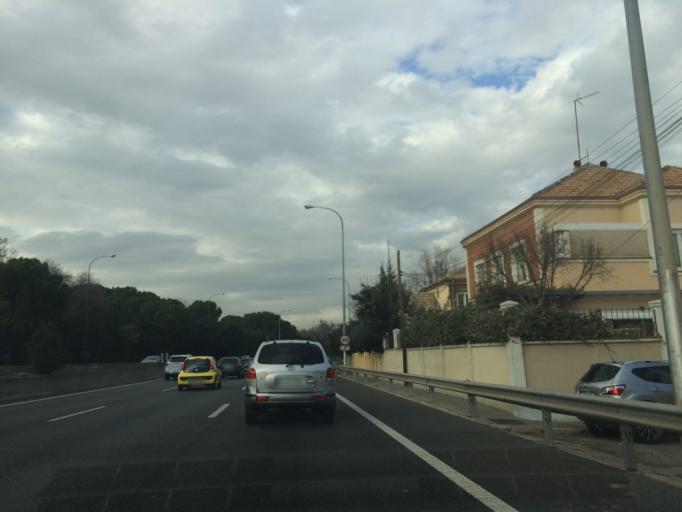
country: ES
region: Madrid
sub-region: Provincia de Madrid
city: Moncloa-Aravaca
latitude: 40.4294
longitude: -3.7361
